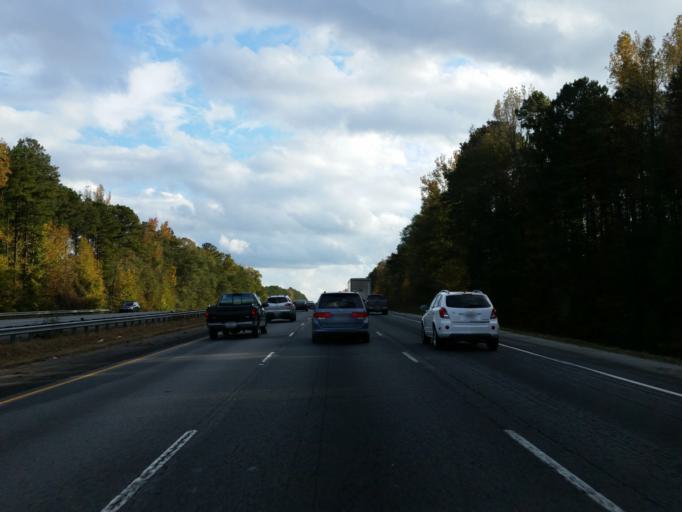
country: US
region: Georgia
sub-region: Henry County
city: Locust Grove
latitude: 33.2954
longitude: -84.1115
